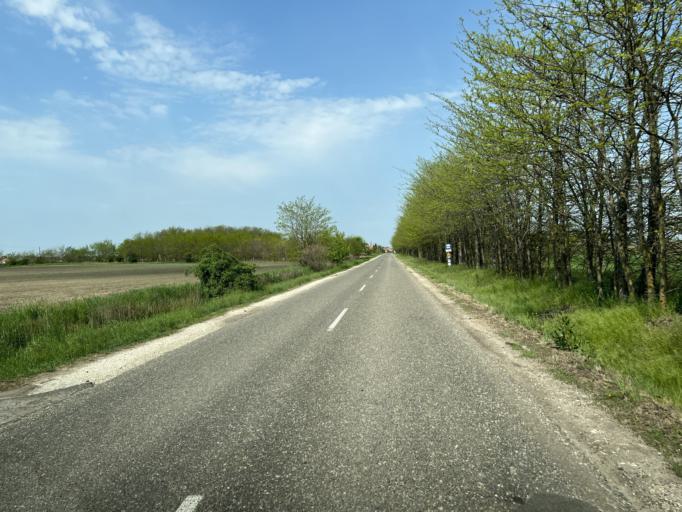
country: HU
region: Pest
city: Tortel
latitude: 47.1175
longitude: 19.9559
